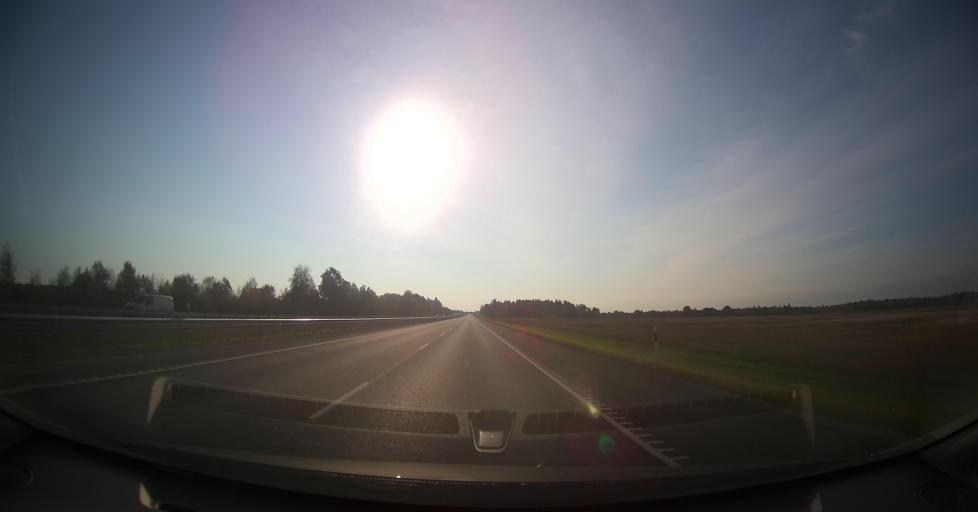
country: EE
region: Harju
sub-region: Rae vald
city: Vaida
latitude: 59.2648
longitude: 24.9928
